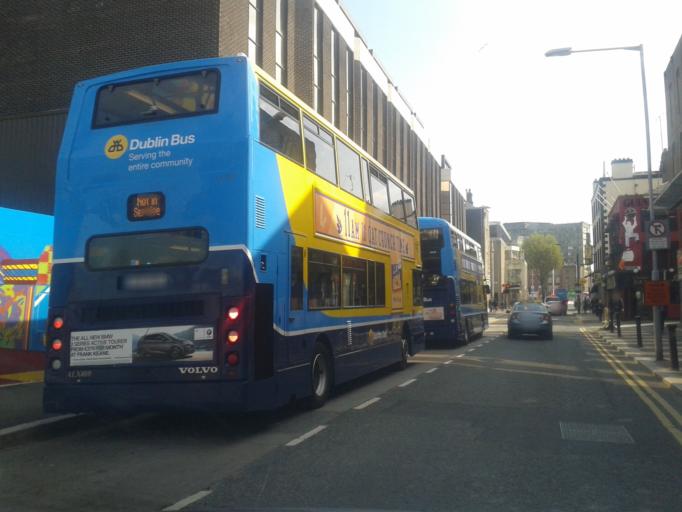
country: IE
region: Leinster
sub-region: Dublin City
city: Dublin
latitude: 53.3497
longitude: -6.2580
